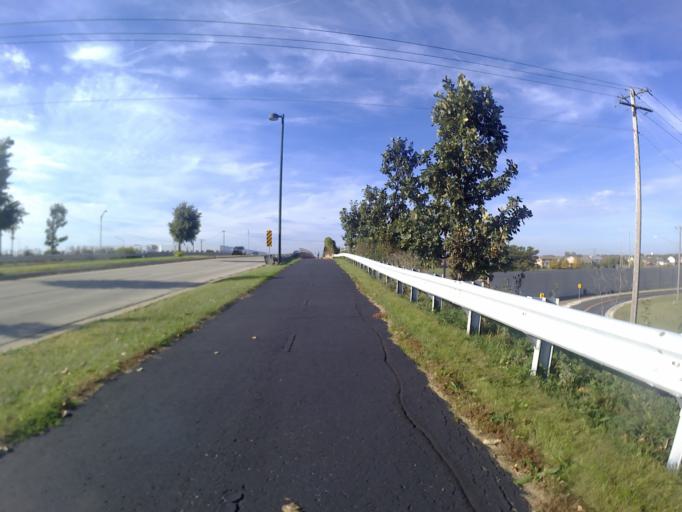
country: US
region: Illinois
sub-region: Cook County
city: Lemont
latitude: 41.7069
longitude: -88.0237
